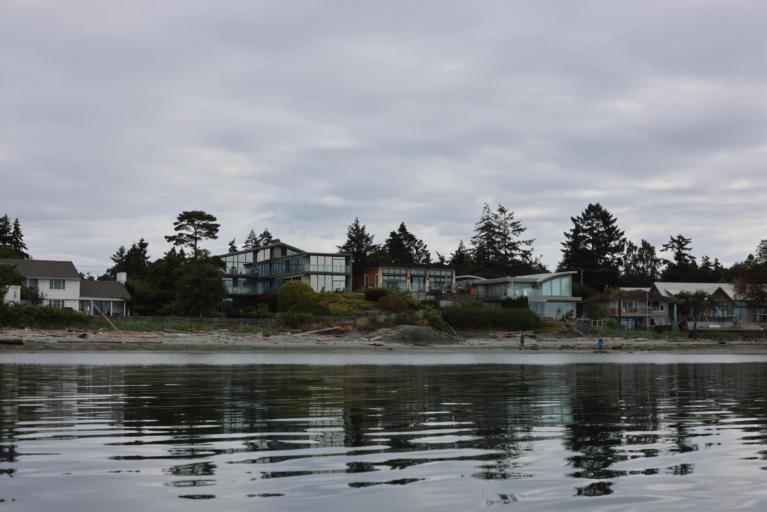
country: CA
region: British Columbia
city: Oak Bay
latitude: 48.4585
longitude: -123.2911
